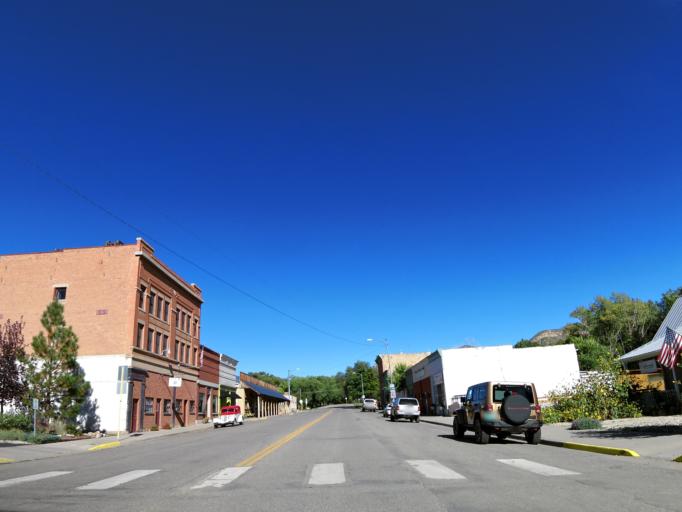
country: US
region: Colorado
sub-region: Montezuma County
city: Mancos
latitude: 37.3451
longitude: -108.2904
